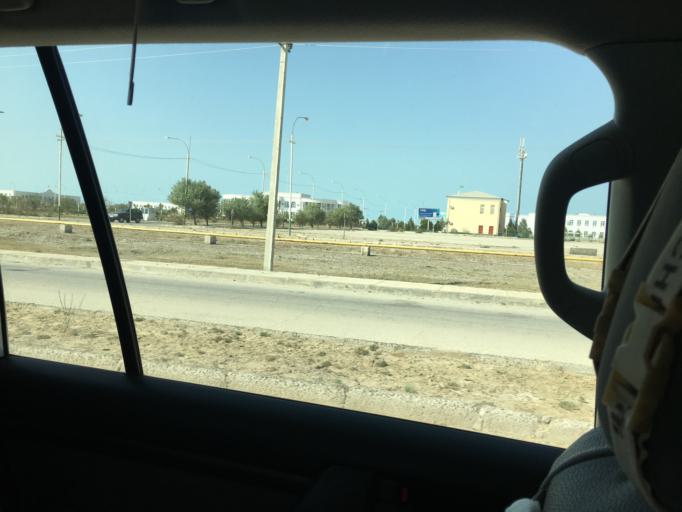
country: IR
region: Golestan
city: Gomishan
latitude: 37.4798
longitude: 53.9765
